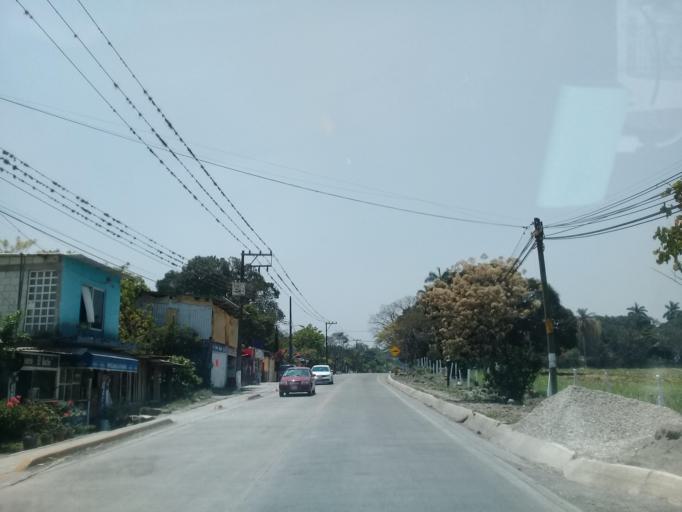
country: MX
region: Veracruz
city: Paraje Nuevo
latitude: 18.8730
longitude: -96.8692
